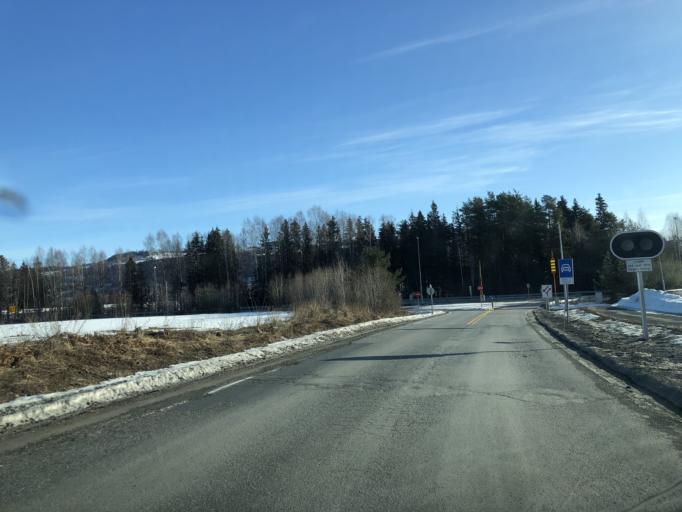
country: NO
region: Hedmark
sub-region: Ringsaker
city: Moelv
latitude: 60.9579
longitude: 10.6211
